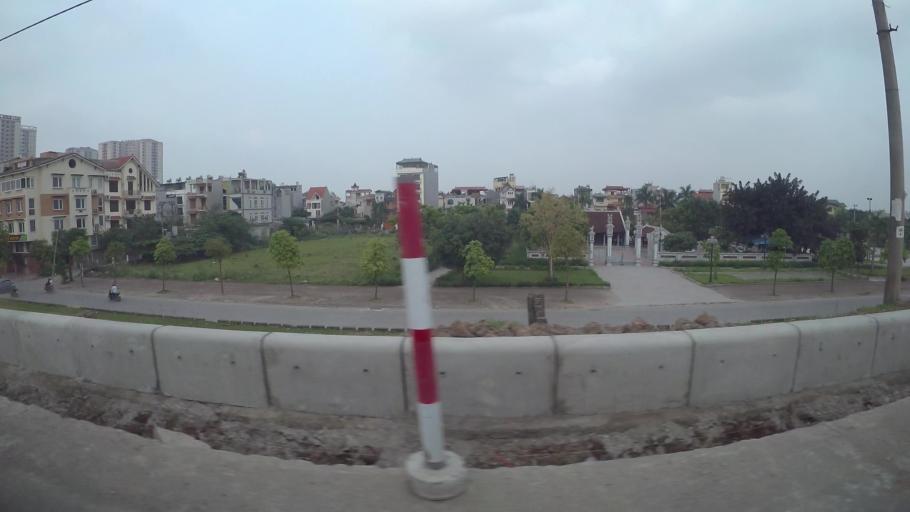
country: VN
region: Ha Noi
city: Trau Quy
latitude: 21.0155
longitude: 105.9048
